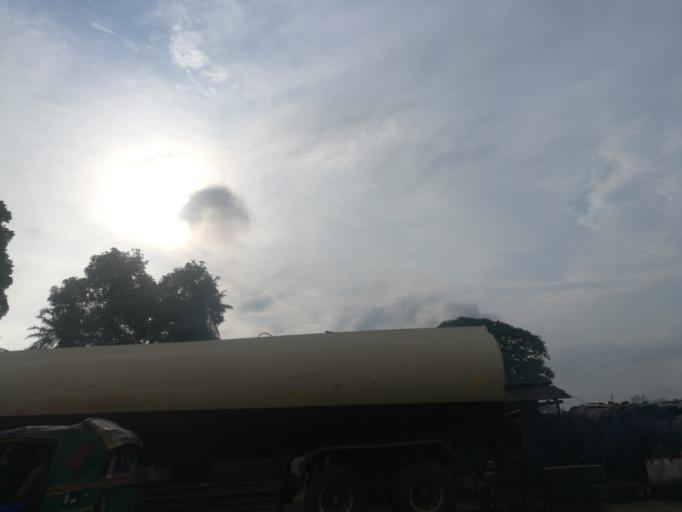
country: NG
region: Rivers
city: Okrika
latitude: 4.7736
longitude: 7.1066
